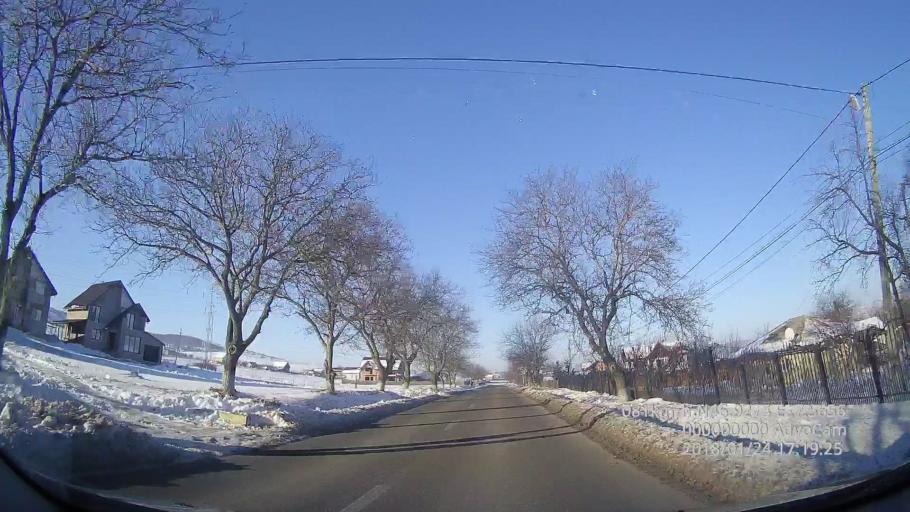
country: RO
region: Iasi
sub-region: Comuna Scanteia
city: Scanteia
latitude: 46.9279
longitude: 27.5635
